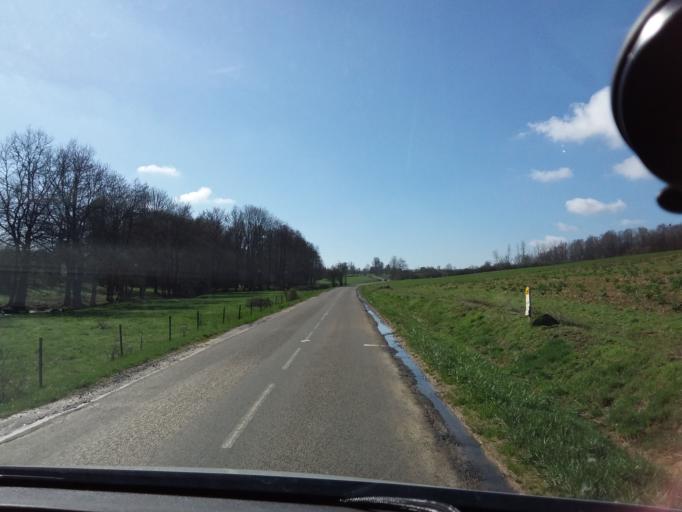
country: FR
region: Picardie
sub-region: Departement de l'Aisne
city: Hirson
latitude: 49.8665
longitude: 4.0903
